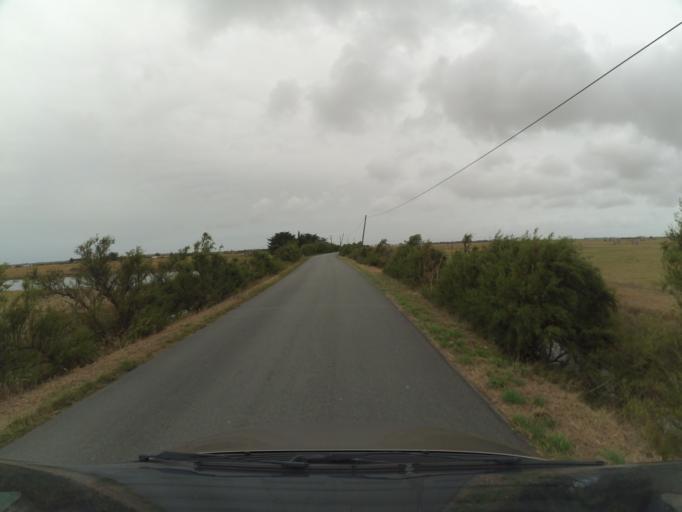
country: FR
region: Pays de la Loire
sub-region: Departement de la Vendee
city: La Barre-de-Monts
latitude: 46.8824
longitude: -2.0846
